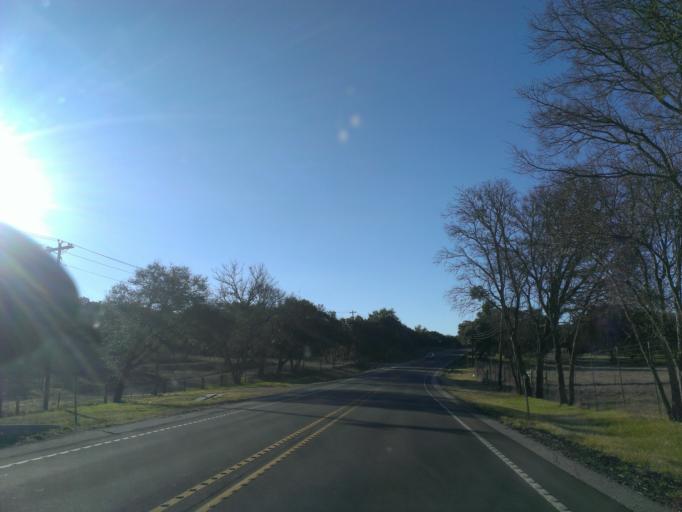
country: US
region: Texas
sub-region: Hays County
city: Dripping Springs
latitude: 30.1401
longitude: -98.0883
